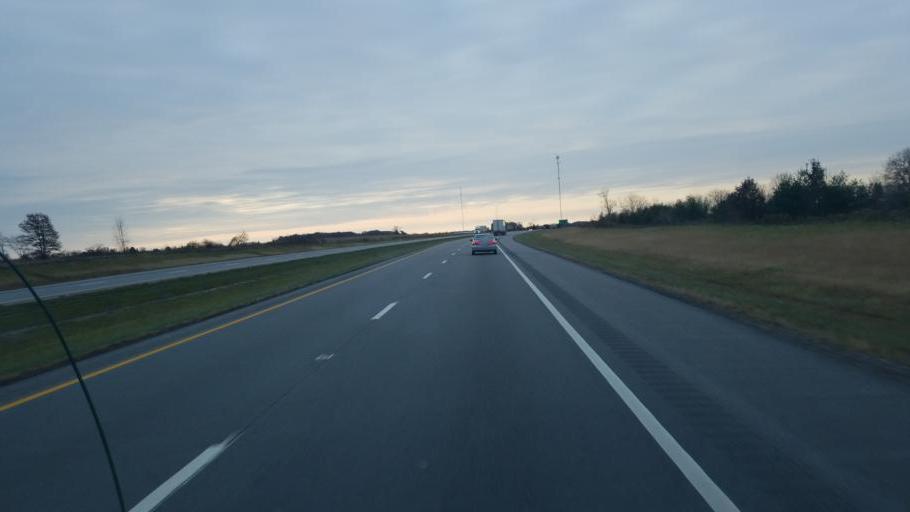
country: US
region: Ohio
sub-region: Auglaize County
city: Cridersville
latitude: 40.6448
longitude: -84.1314
